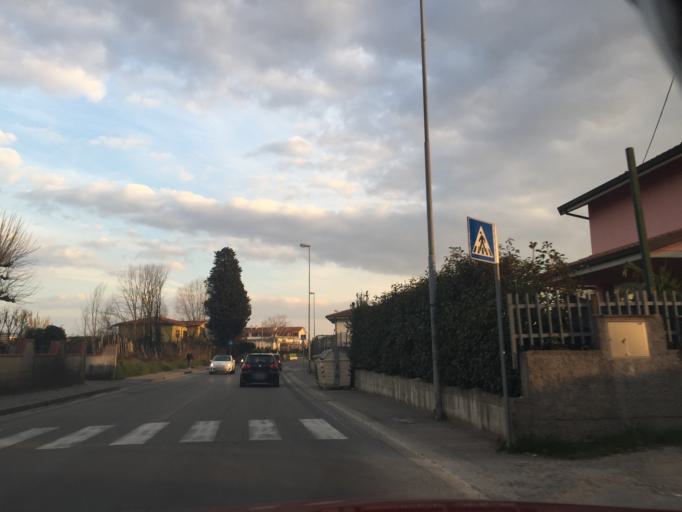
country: IT
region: Tuscany
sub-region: Provincia di Pistoia
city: Borgo a Buggiano
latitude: 43.8690
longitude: 10.7383
